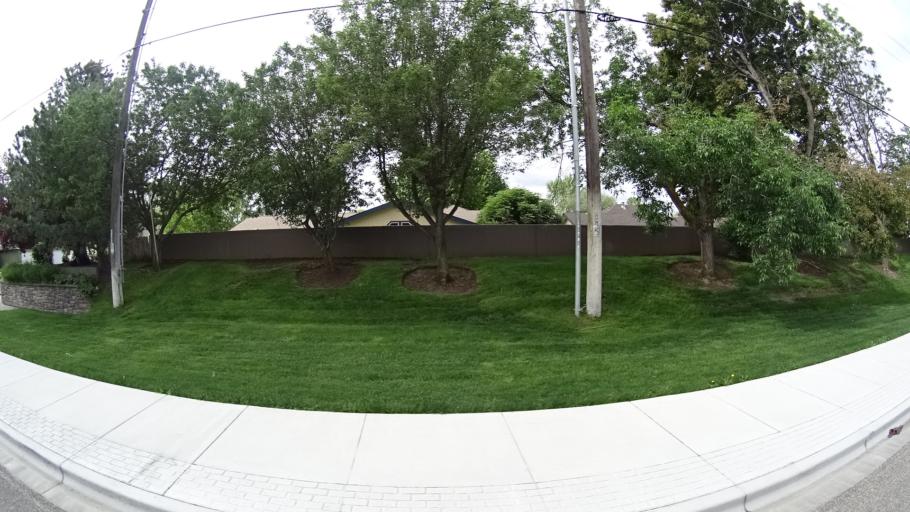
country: US
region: Idaho
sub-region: Ada County
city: Eagle
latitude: 43.6952
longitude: -116.3265
